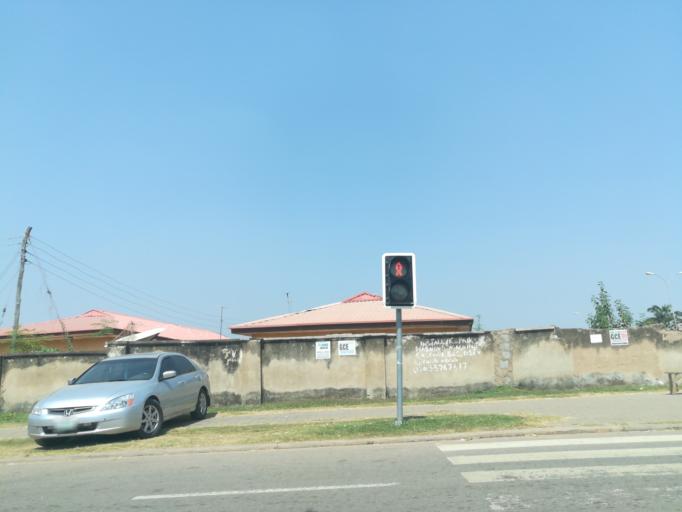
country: NG
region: Abuja Federal Capital Territory
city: Abuja
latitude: 9.0642
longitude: 7.4227
